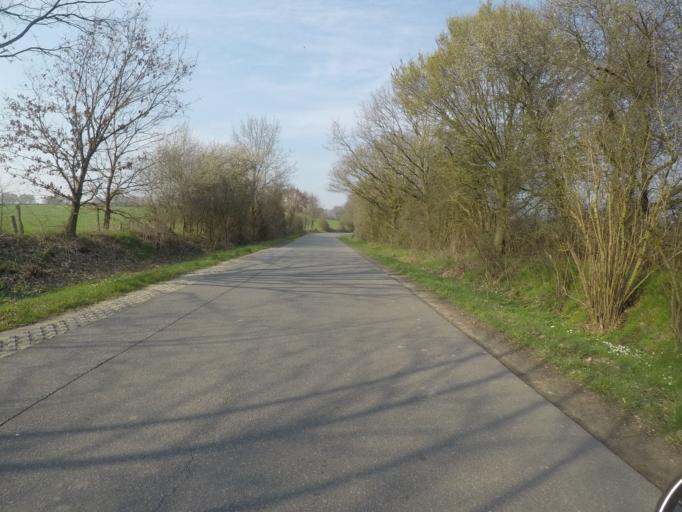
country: DE
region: Schleswig-Holstein
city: Leezen
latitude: 53.8828
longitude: 10.2420
